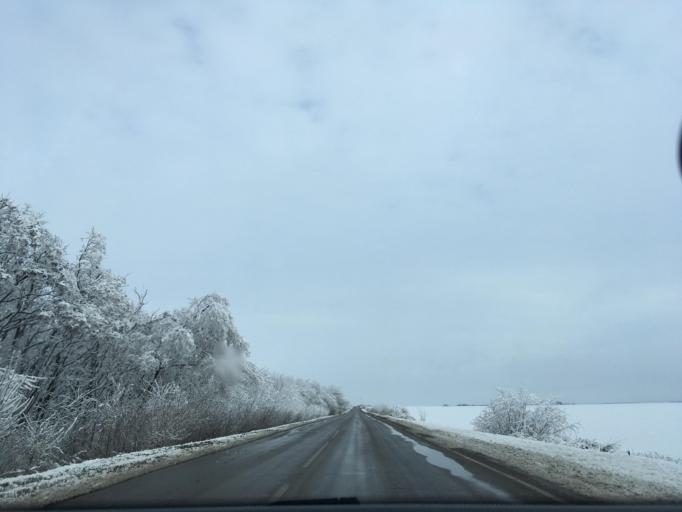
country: UA
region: Luhansk
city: Lozno-Oleksandrivka
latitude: 49.9879
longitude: 39.0132
